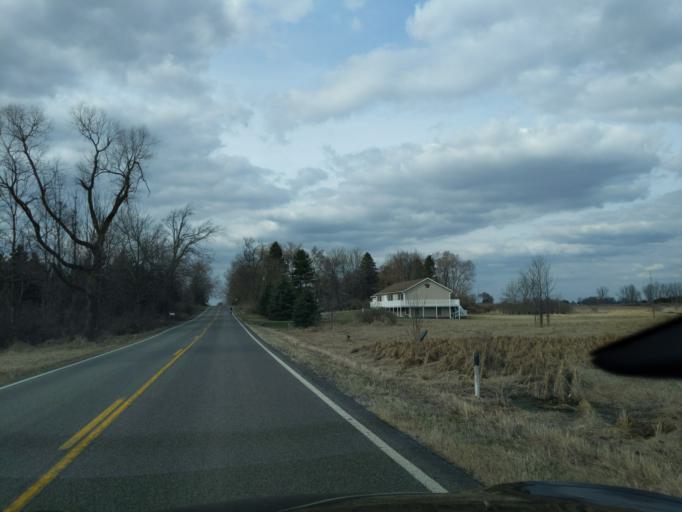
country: US
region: Michigan
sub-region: Ingham County
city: Mason
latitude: 42.5409
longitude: -84.4830
